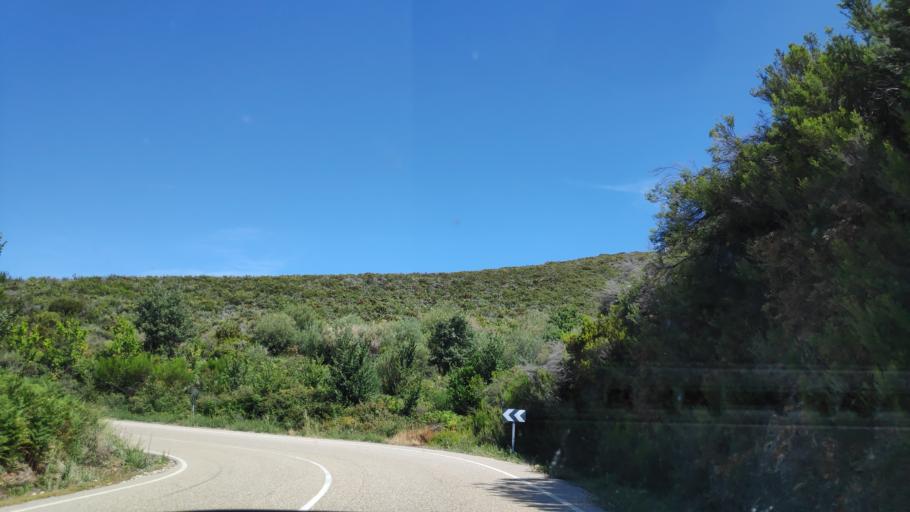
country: ES
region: Castille and Leon
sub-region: Provincia de Zamora
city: Requejo
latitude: 41.9767
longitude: -6.7128
